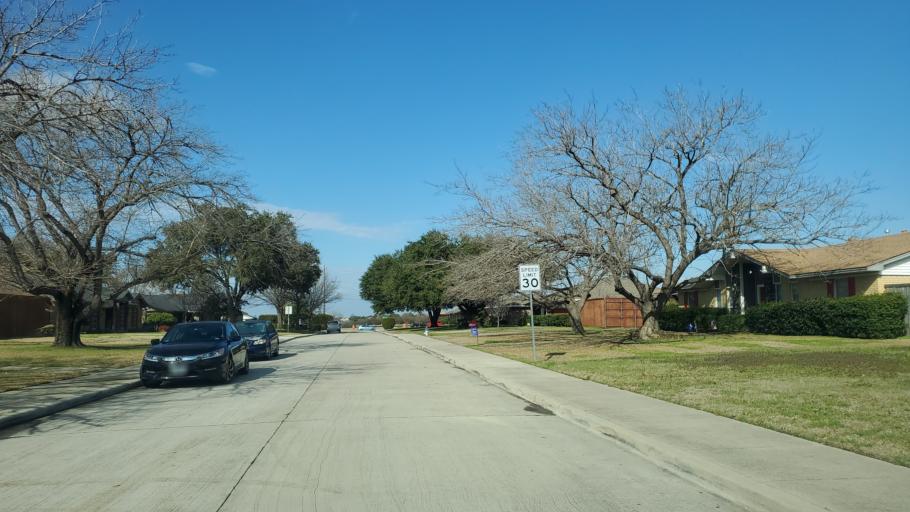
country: US
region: Texas
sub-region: Dallas County
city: Carrollton
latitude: 32.9831
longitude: -96.8922
